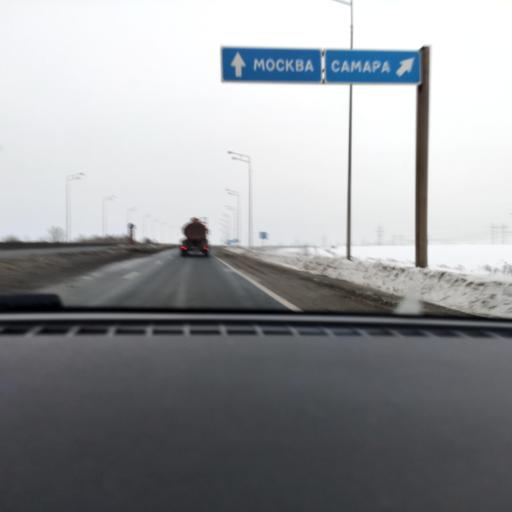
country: RU
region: Samara
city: Smyshlyayevka
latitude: 53.1296
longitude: 50.4225
